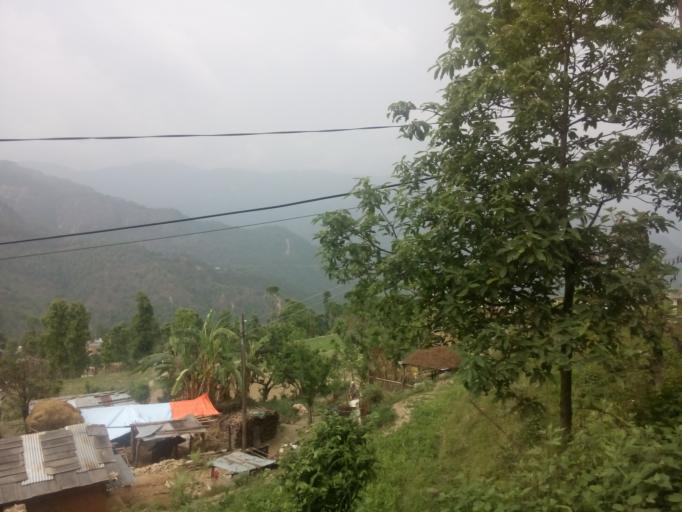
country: NP
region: Central Region
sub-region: Bagmati Zone
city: Nagarkot
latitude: 27.7715
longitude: 85.7214
